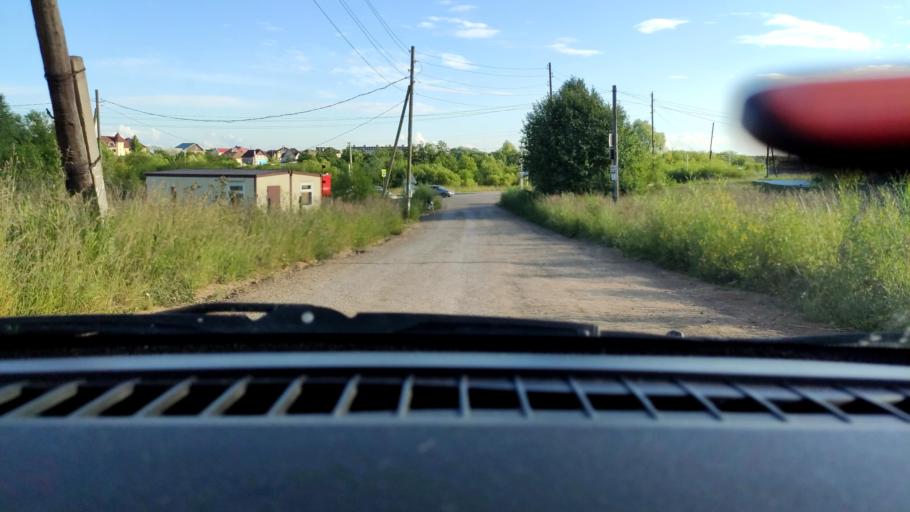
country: RU
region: Perm
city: Kultayevo
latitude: 57.9007
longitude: 55.9263
